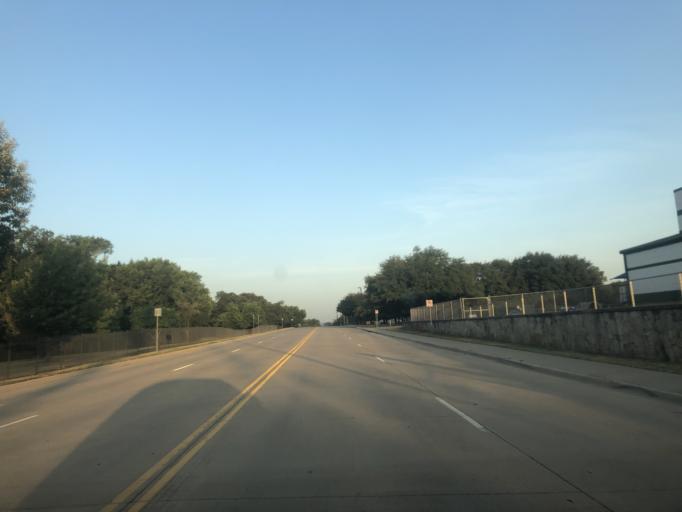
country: US
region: Texas
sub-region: Tarrant County
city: Lake Worth
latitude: 32.8103
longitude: -97.4375
